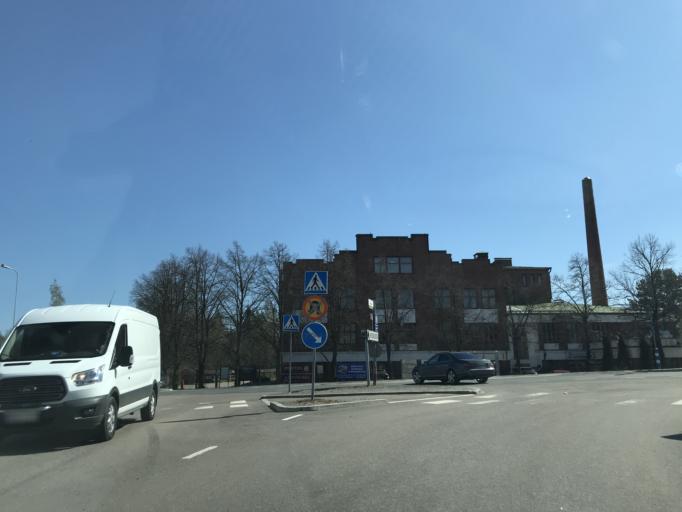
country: FI
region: Paijanne Tavastia
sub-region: Lahti
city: Orimattila
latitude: 60.8022
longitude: 25.7349
